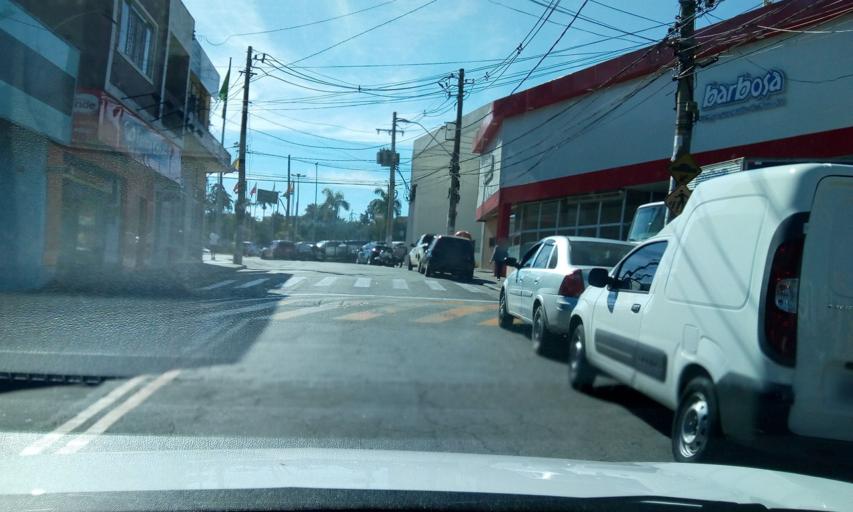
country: BR
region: Sao Paulo
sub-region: Barueri
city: Barueri
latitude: -23.5070
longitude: -46.8756
